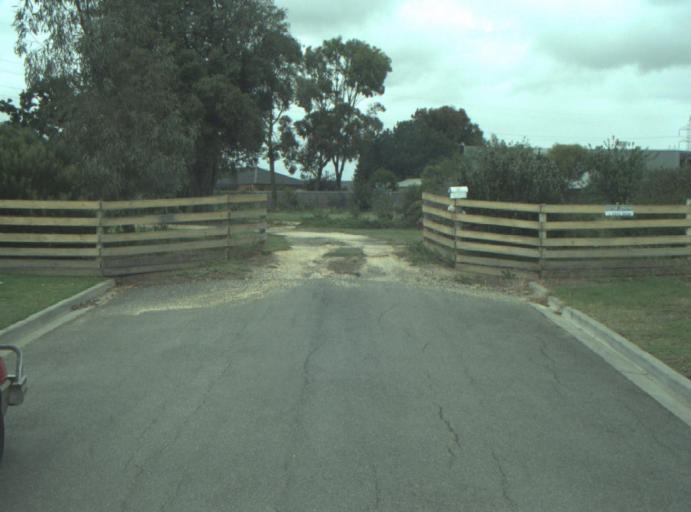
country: AU
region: Victoria
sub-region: Greater Geelong
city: Breakwater
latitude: -38.1977
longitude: 144.3496
